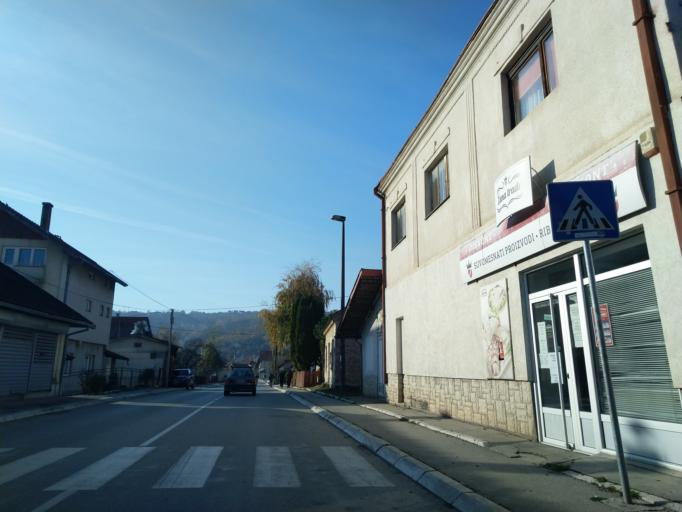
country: RS
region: Central Serbia
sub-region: Zlatiborski Okrug
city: Uzice
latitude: 43.8453
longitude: 19.8947
